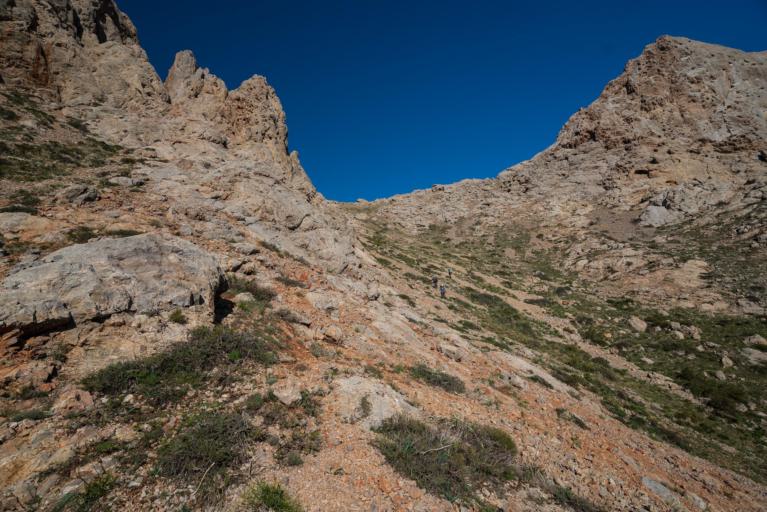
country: KZ
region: Ongtustik Qazaqstan
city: Ashchysay
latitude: 43.7621
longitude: 68.7807
